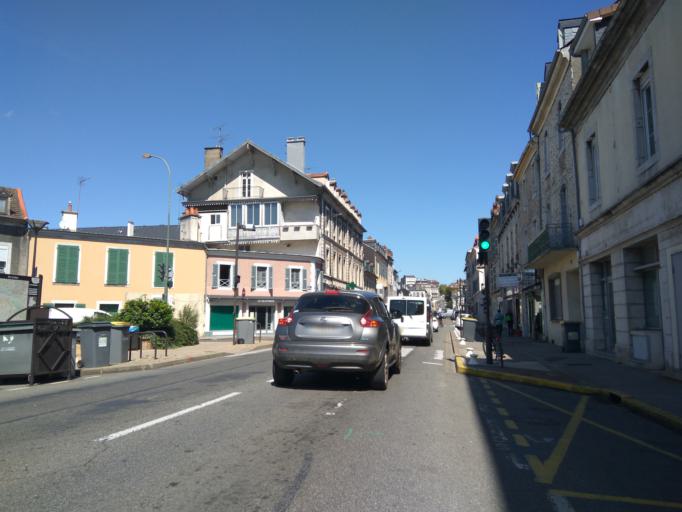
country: FR
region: Aquitaine
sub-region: Departement des Pyrenees-Atlantiques
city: Jurancon
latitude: 43.2915
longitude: -0.3785
